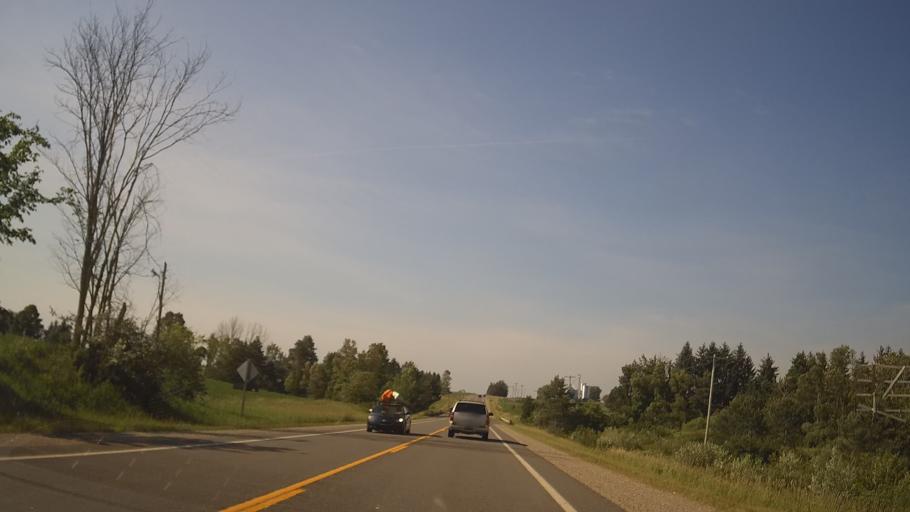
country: US
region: Michigan
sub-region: Ogemaw County
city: West Branch
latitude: 44.3514
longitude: -84.1259
